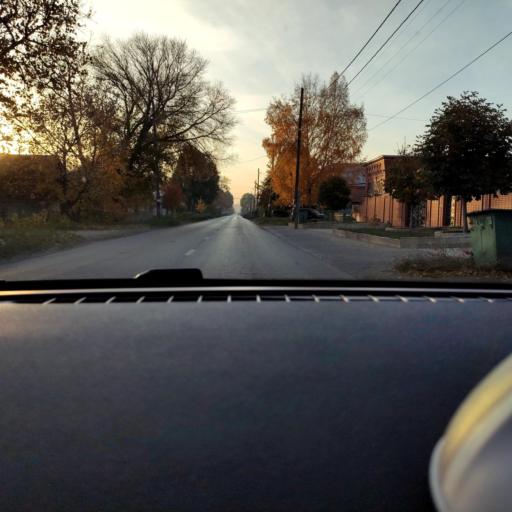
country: RU
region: Samara
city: Petra-Dubrava
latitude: 53.2544
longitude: 50.3267
